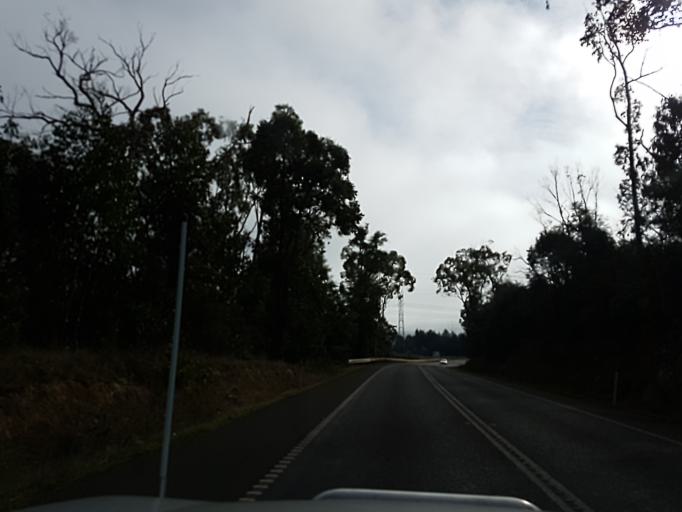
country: AU
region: Victoria
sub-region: Murrindindi
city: Kinglake West
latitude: -37.4523
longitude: 145.4183
